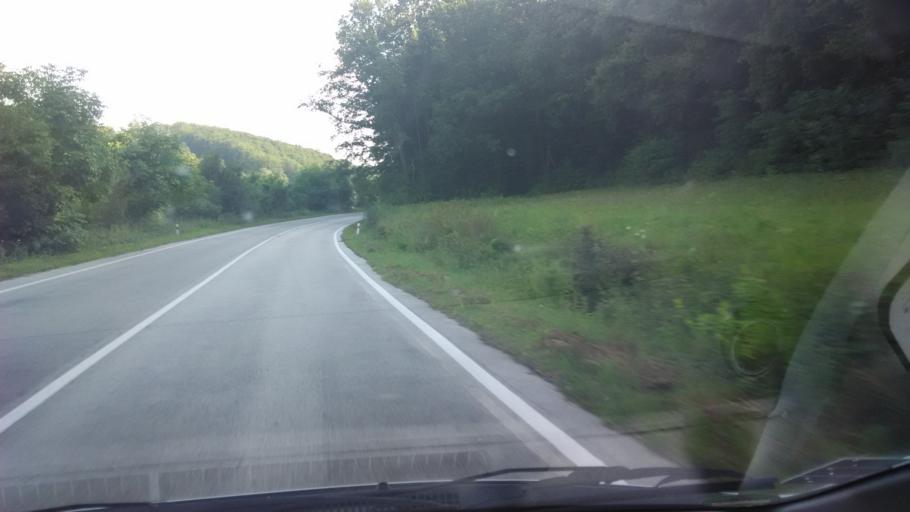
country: SK
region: Nitriansky
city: Zlate Moravce
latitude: 48.4479
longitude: 18.4130
